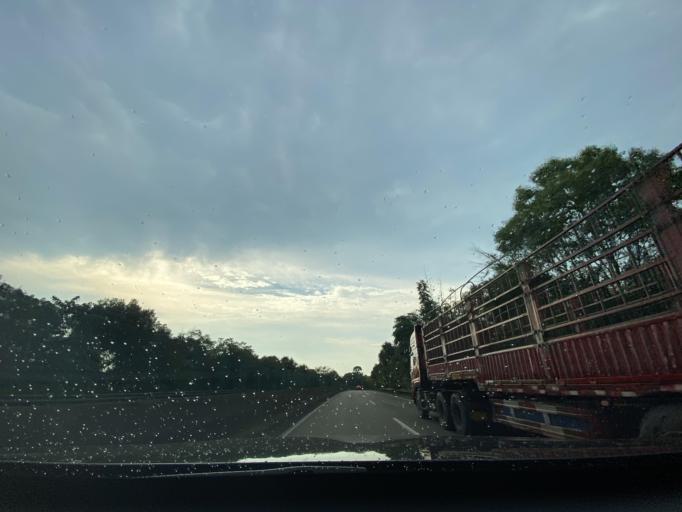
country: CN
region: Sichuan
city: Chonglong
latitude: 29.7889
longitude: 104.7292
